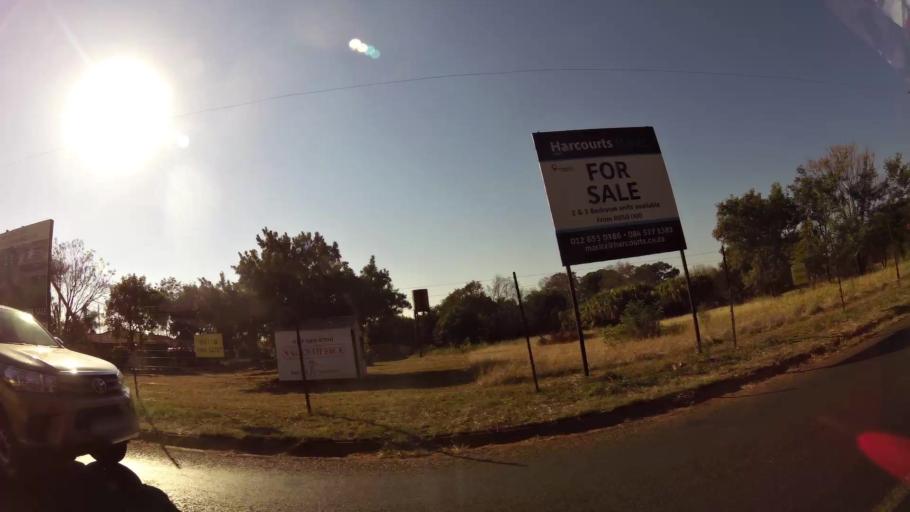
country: ZA
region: Gauteng
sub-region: City of Tshwane Metropolitan Municipality
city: Pretoria
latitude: -25.6582
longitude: 28.1317
